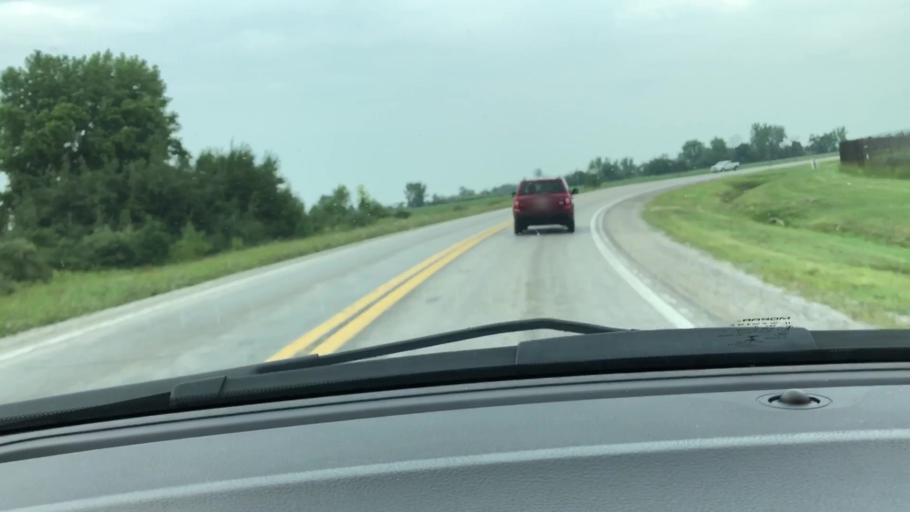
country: US
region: Michigan
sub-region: Saginaw County
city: Freeland
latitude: 43.5385
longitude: -84.0956
